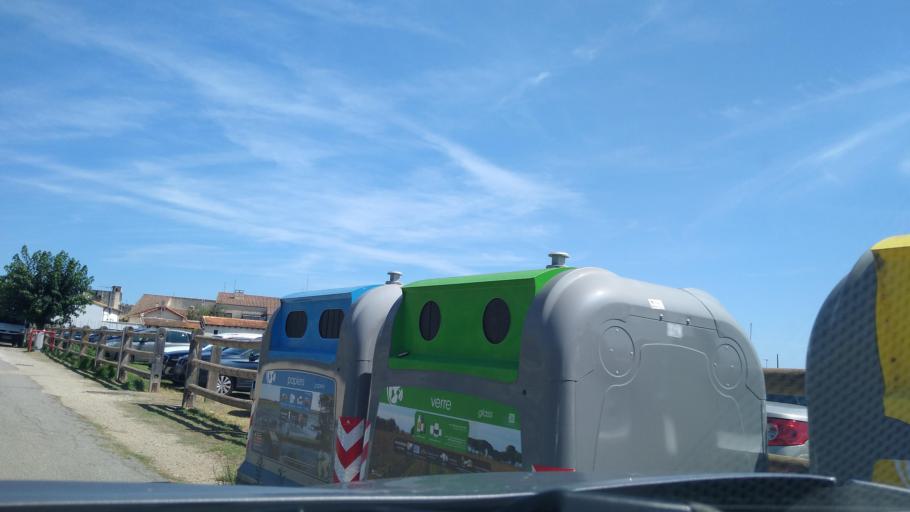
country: FR
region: Languedoc-Roussillon
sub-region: Departement du Gard
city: Aigues-Mortes
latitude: 43.5679
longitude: 4.1853
